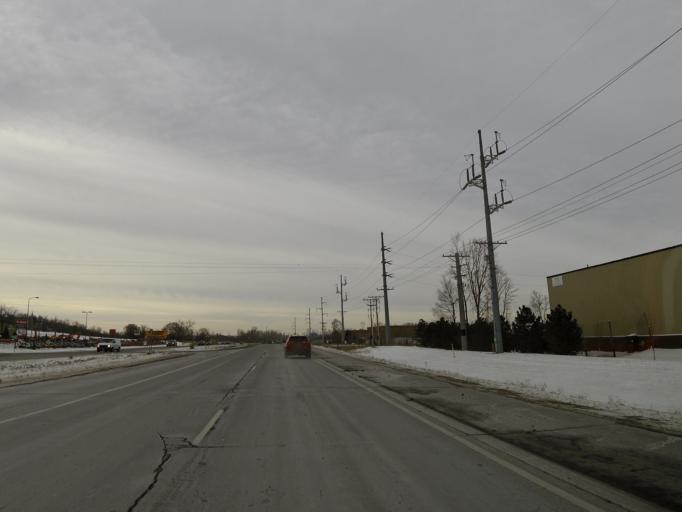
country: US
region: Minnesota
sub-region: Carver County
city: Chaska
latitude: 44.7591
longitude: -93.5834
